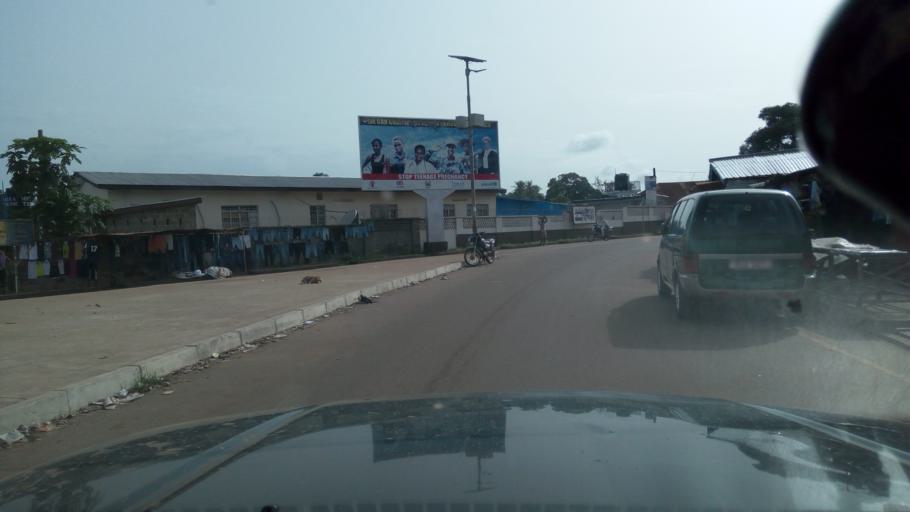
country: SL
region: Northern Province
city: Port Loko
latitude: 8.7646
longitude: -12.7851
